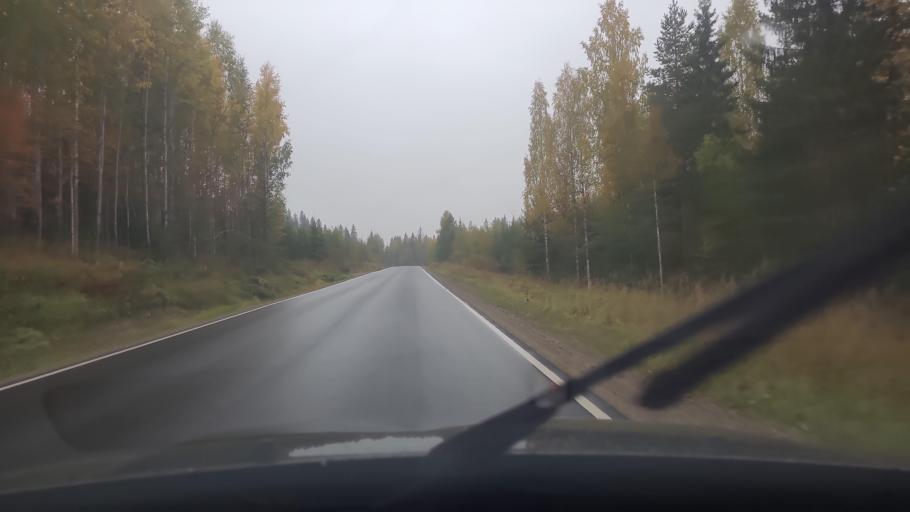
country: FI
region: Northern Savo
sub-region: Varkaus
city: Kangaslampi
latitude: 62.4579
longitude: 28.2676
